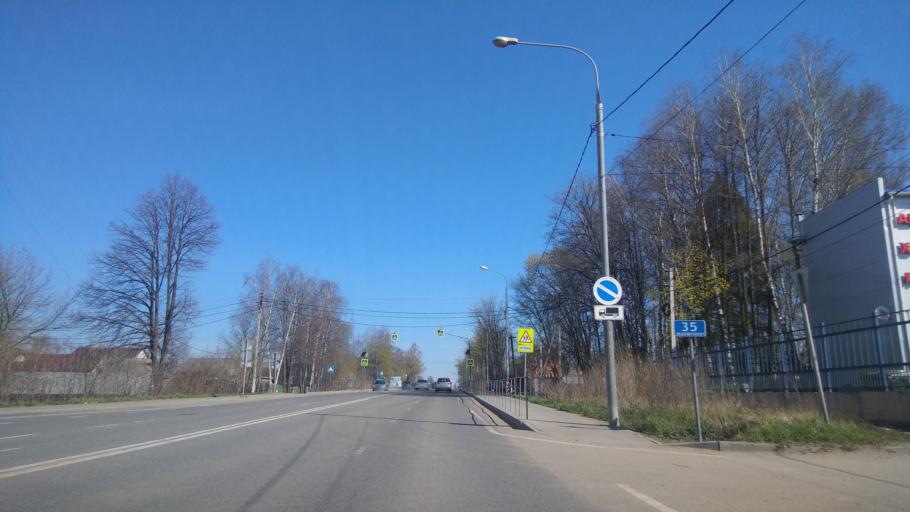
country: RU
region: Moskovskaya
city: Pushkino
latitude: 56.0138
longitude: 37.8720
